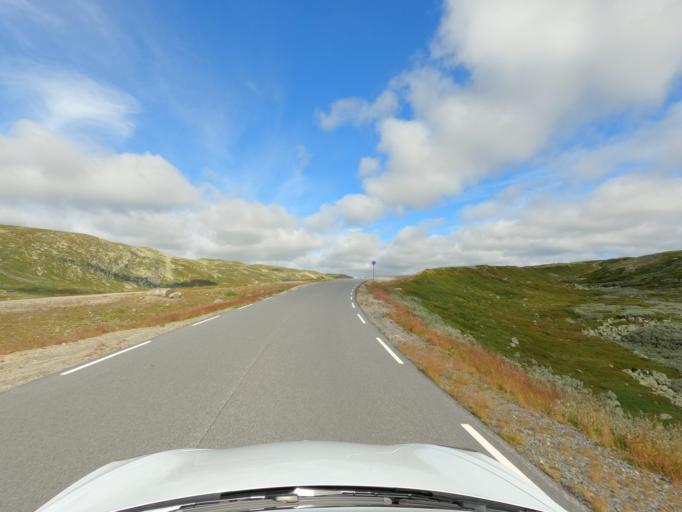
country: NO
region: Telemark
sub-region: Tinn
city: Rjukan
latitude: 60.1551
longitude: 8.6118
